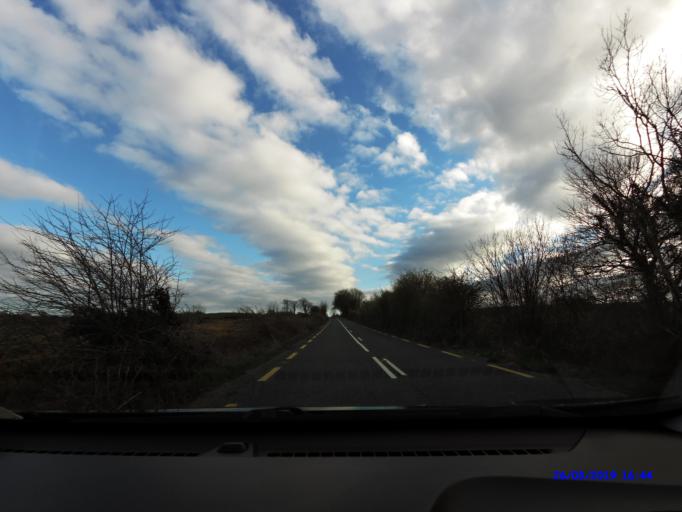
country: IE
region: Connaught
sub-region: Maigh Eo
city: Ballyhaunis
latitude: 53.8456
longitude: -8.7654
